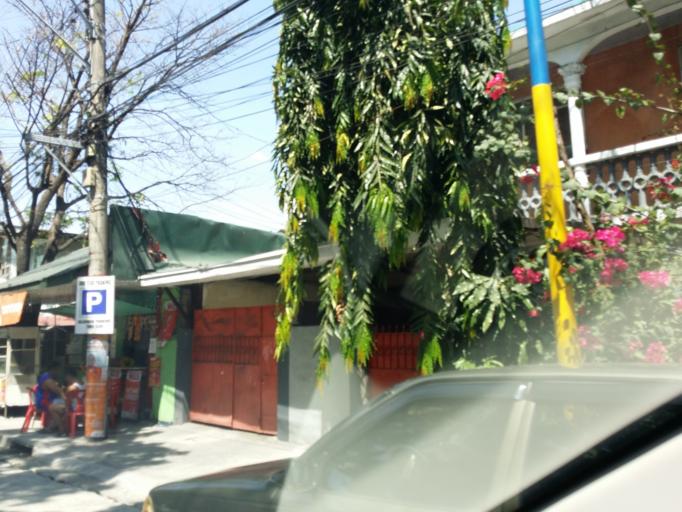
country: PH
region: Metro Manila
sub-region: Mandaluyong
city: Mandaluyong City
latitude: 14.5870
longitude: 121.0299
